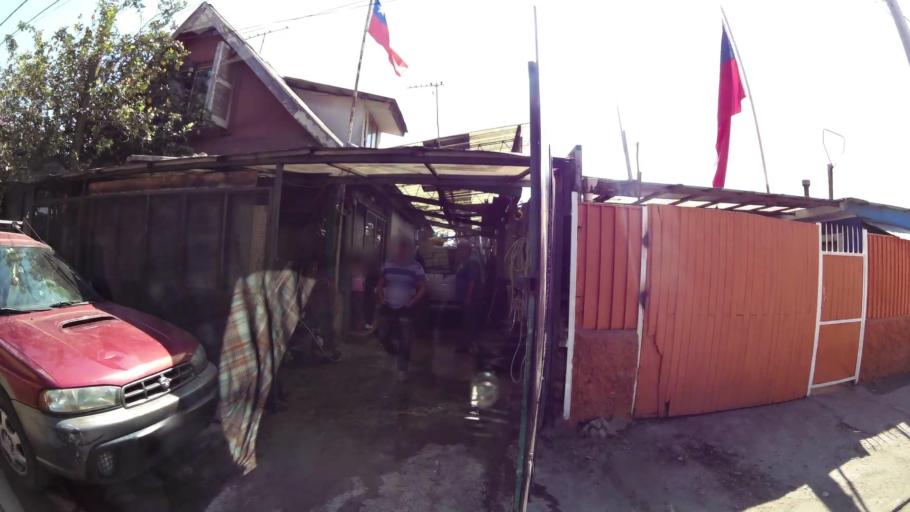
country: CL
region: Santiago Metropolitan
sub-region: Provincia de Santiago
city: Lo Prado
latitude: -33.3952
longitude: -70.6993
